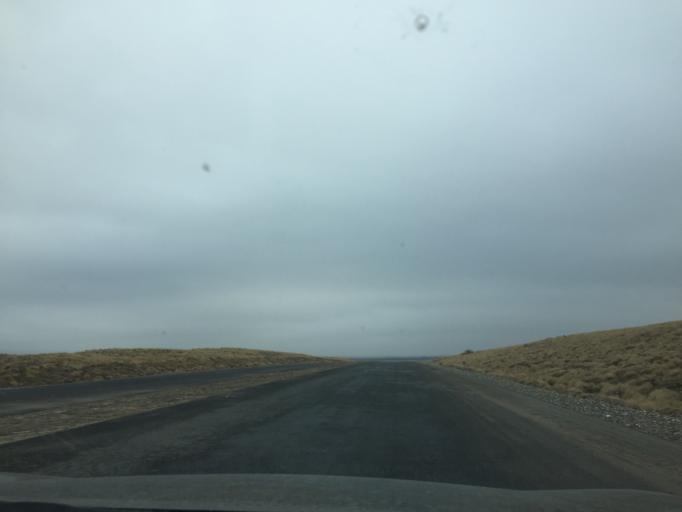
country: KZ
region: Ongtustik Qazaqstan
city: Kokterek
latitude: 42.5448
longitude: 70.1831
